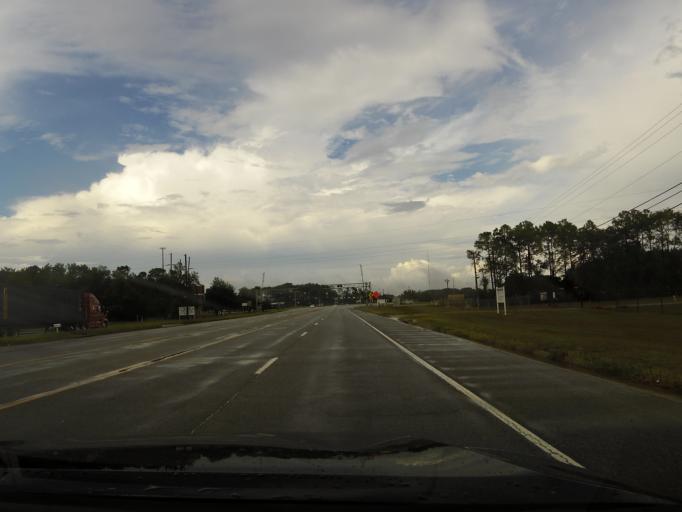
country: US
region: Georgia
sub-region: Wayne County
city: Jesup
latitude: 31.6583
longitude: -81.8500
